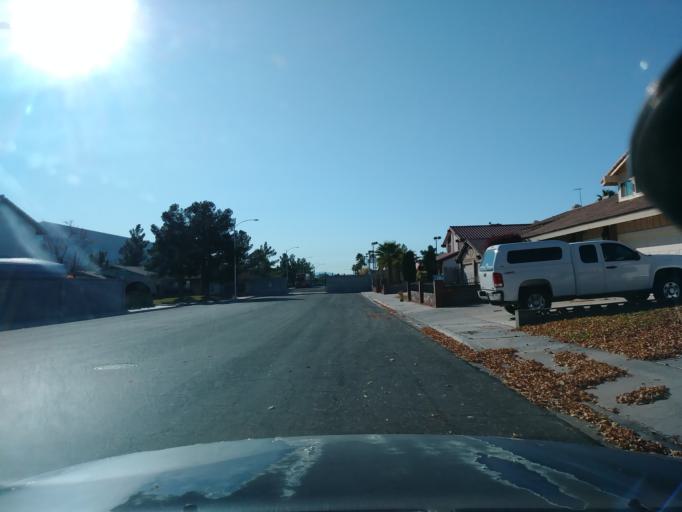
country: US
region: Nevada
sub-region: Clark County
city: Spring Valley
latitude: 36.1469
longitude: -115.2298
